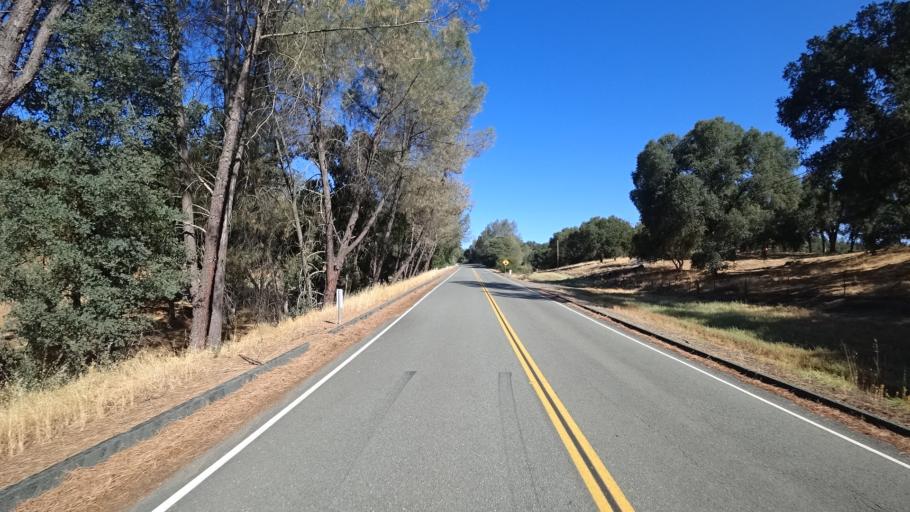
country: US
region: California
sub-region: Calaveras County
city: San Andreas
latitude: 38.2273
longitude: -120.7016
